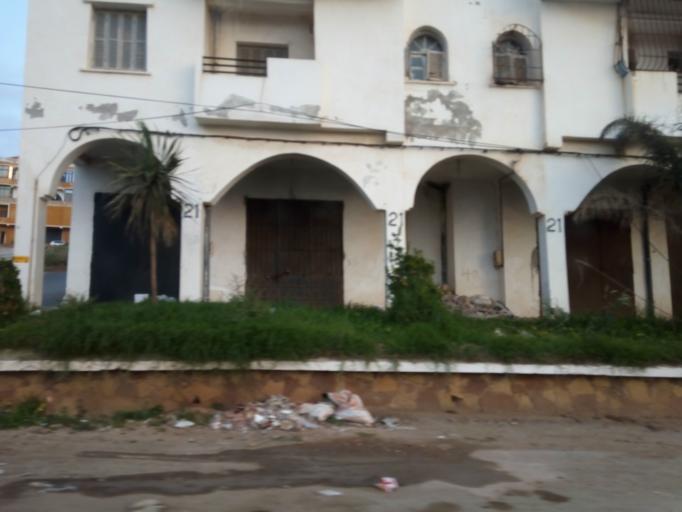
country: DZ
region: Tipaza
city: Bou Ismail
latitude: 36.6068
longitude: 2.6183
